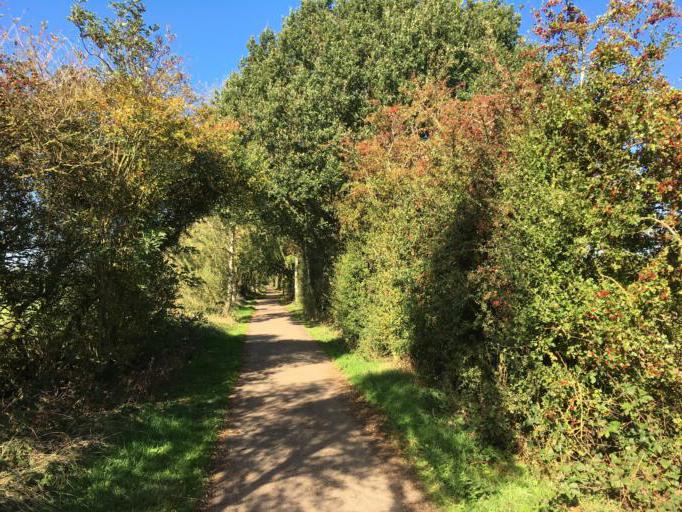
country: GB
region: England
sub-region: Warwickshire
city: Kenilworth
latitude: 52.3689
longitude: -1.5864
